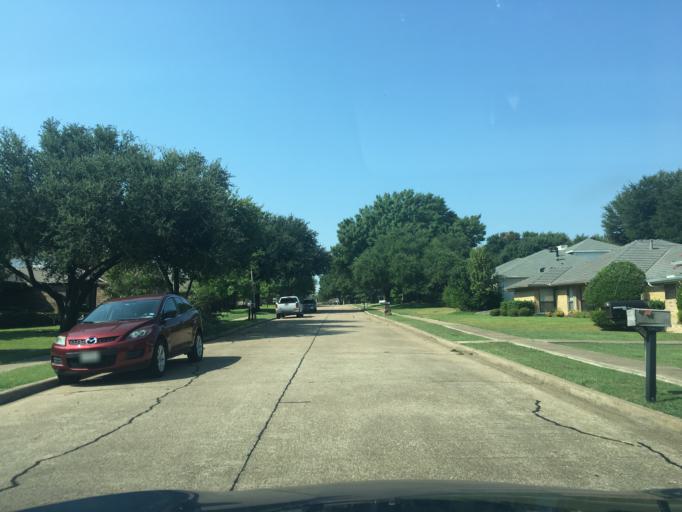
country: US
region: Texas
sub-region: Dallas County
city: Garland
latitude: 32.9491
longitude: -96.6326
